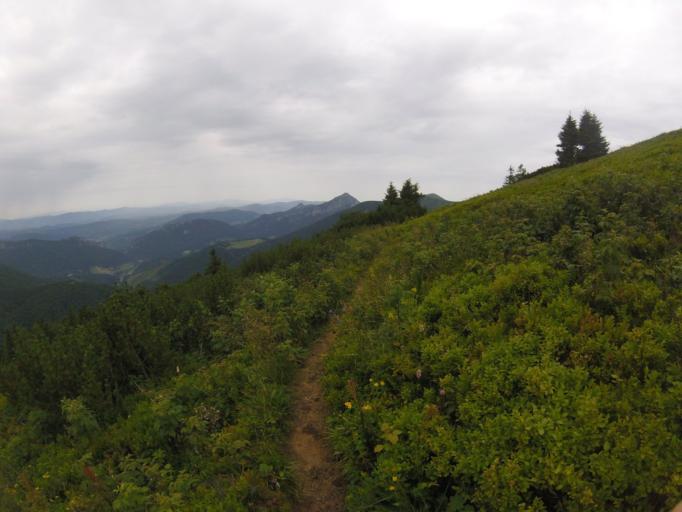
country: SK
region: Zilinsky
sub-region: Okres Zilina
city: Terchova
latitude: 49.1944
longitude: 19.0260
